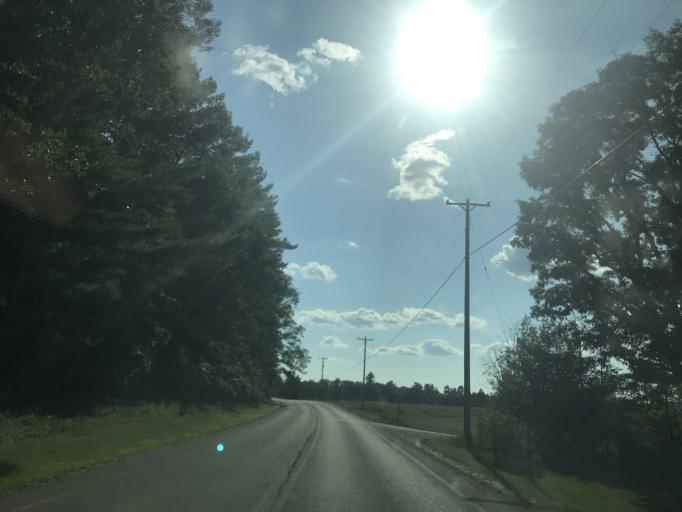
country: US
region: Michigan
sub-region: Newaygo County
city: Newaygo
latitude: 43.4263
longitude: -85.7839
